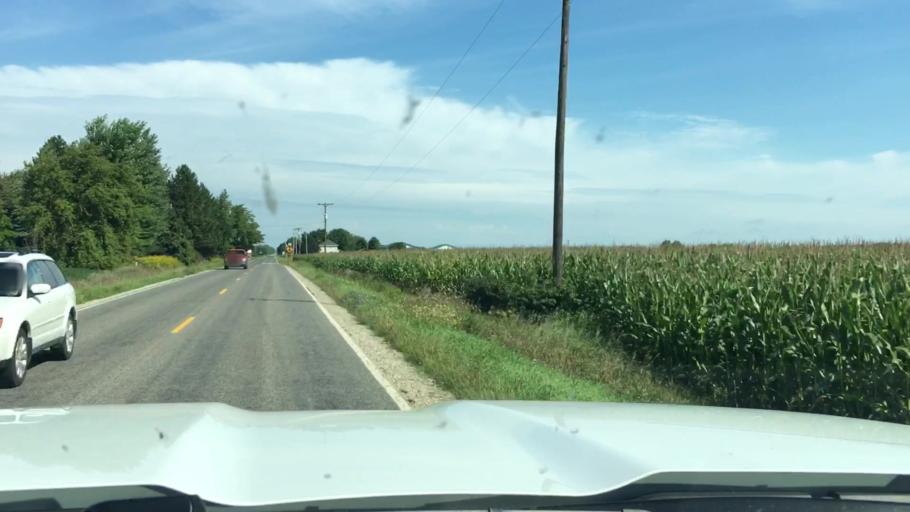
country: US
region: Michigan
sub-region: Midland County
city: Midland
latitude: 43.5220
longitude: -84.2294
